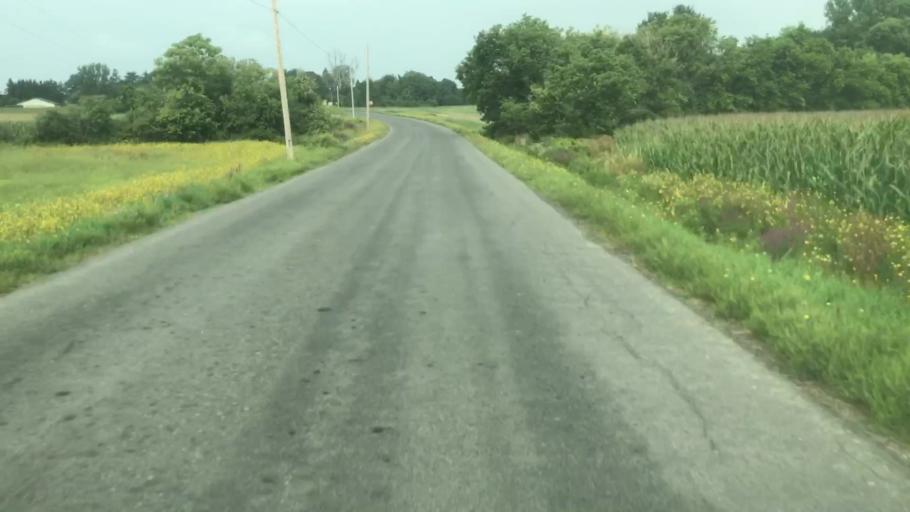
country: US
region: New York
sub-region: Onondaga County
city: Skaneateles
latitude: 42.9031
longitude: -76.4625
